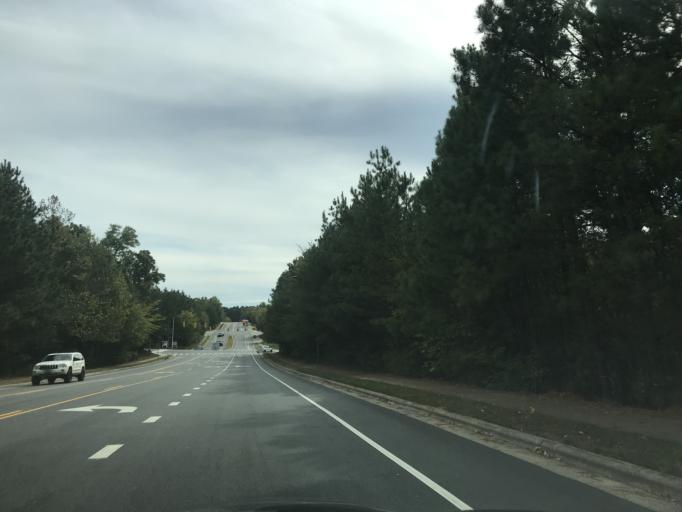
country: US
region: North Carolina
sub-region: Wake County
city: Wake Forest
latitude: 35.9472
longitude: -78.5451
